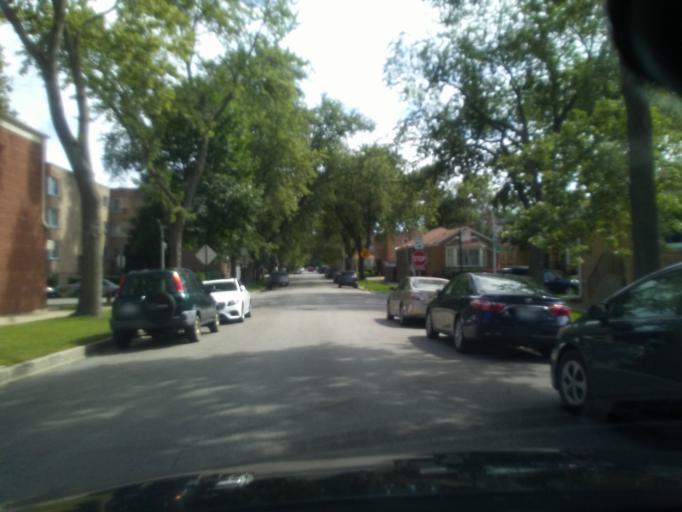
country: US
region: Illinois
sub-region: Cook County
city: Lincolnwood
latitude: 41.9956
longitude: -87.7085
